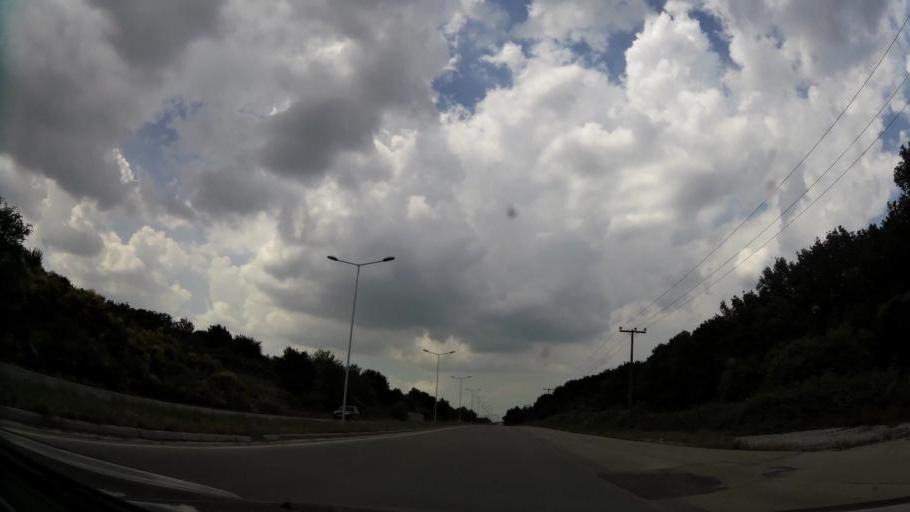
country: GR
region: West Macedonia
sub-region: Nomos Kozanis
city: Koila
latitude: 40.3204
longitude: 21.8279
